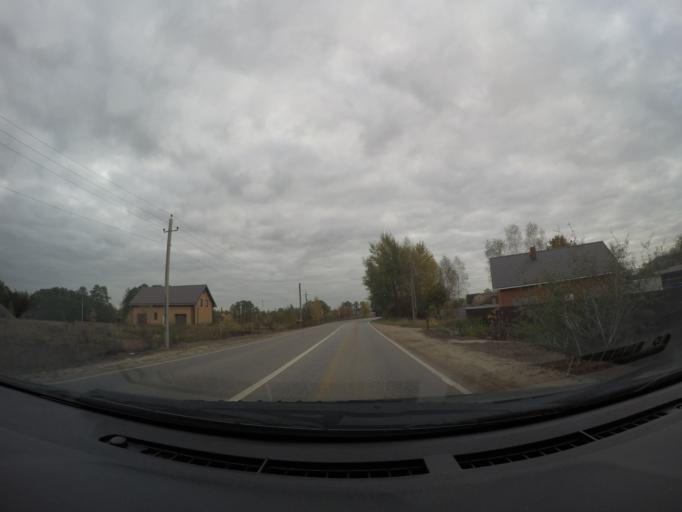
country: RU
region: Moskovskaya
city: Gzhel'
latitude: 55.6425
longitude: 38.3751
